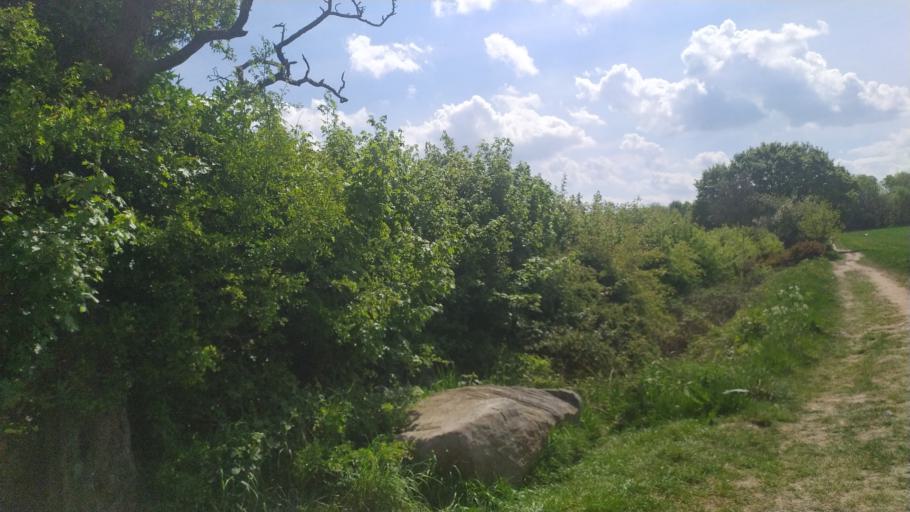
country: GB
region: England
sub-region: City and Borough of Leeds
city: Chapel Allerton
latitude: 53.8839
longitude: -1.5451
